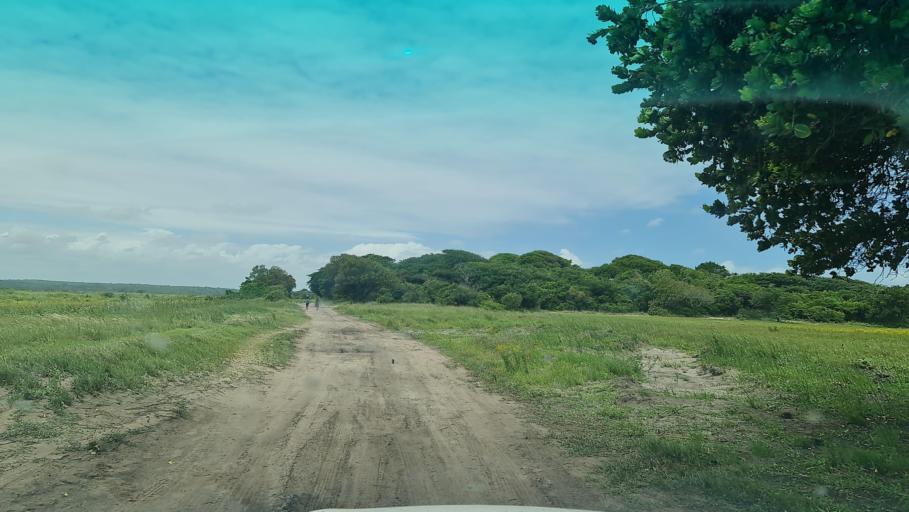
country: MZ
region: Maputo
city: Manhica
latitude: -25.5285
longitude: 32.8504
